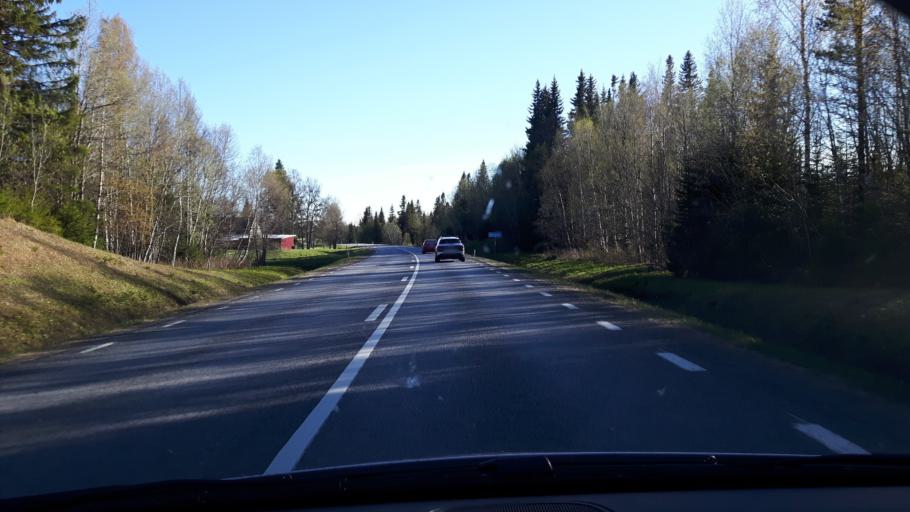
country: SE
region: Jaemtland
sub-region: OEstersunds Kommun
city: Lit
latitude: 63.4383
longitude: 15.1275
